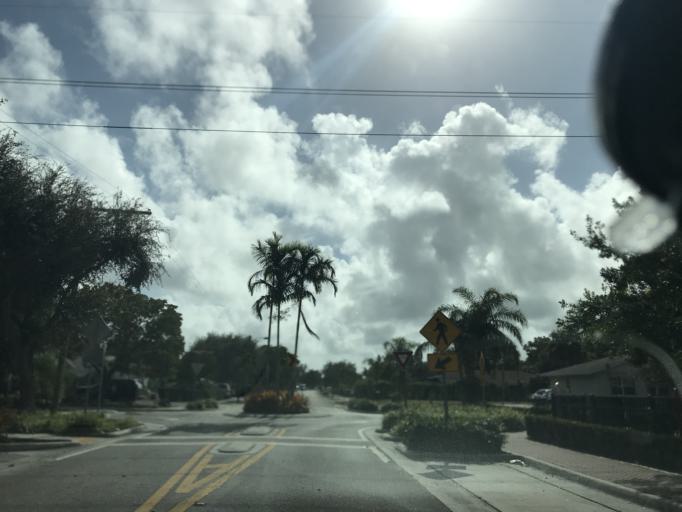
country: US
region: Florida
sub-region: Palm Beach County
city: Delray Beach
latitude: 26.4601
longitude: -80.0822
